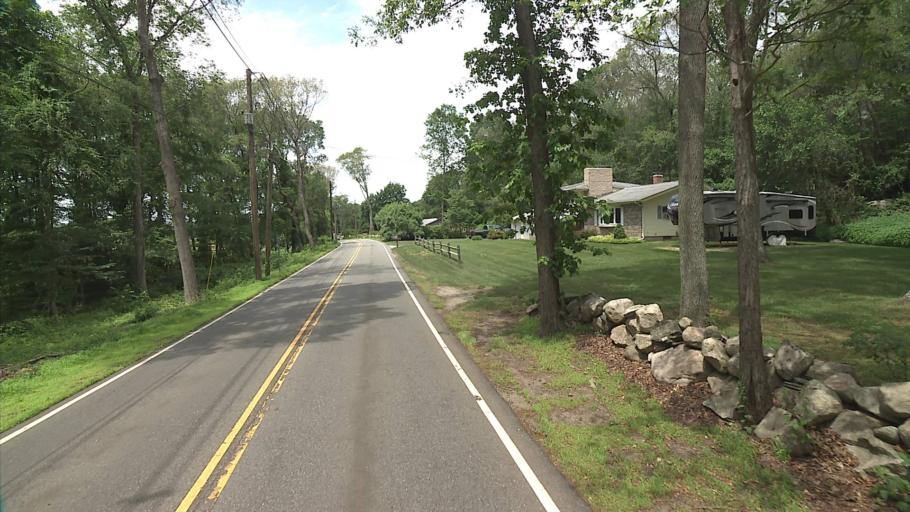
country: US
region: Connecticut
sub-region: New London County
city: Gales Ferry
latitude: 41.4534
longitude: -72.0633
